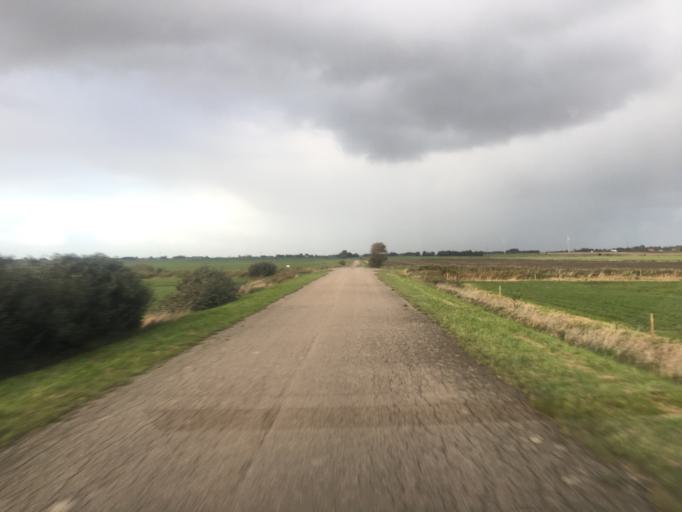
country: DE
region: Schleswig-Holstein
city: Aventoft
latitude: 54.9311
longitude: 8.7749
